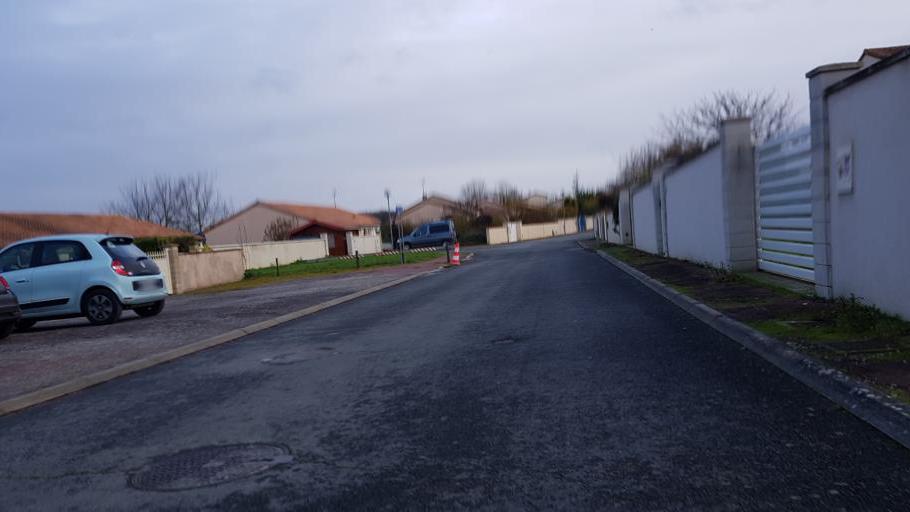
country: FR
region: Poitou-Charentes
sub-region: Departement de la Vienne
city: Avanton
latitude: 46.6642
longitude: 0.3144
